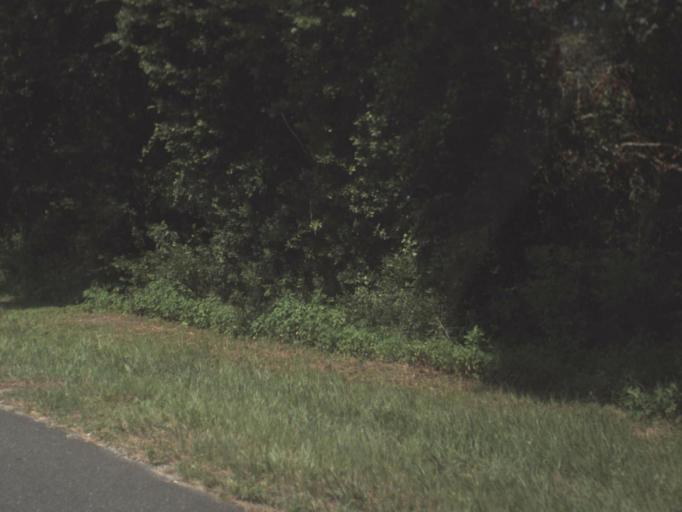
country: US
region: Florida
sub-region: Union County
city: Lake Butler
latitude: 29.9588
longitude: -82.4111
